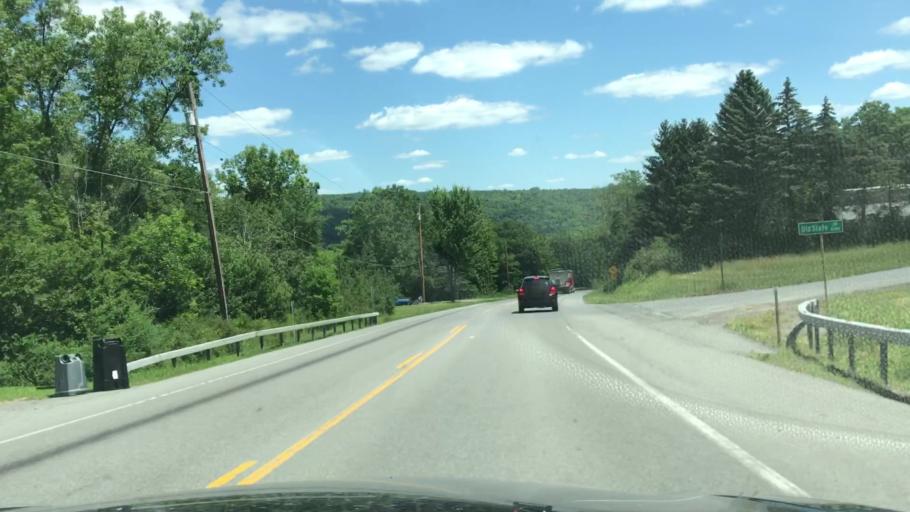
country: US
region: New York
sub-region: Wyoming County
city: Attica
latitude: 42.7701
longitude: -78.3254
